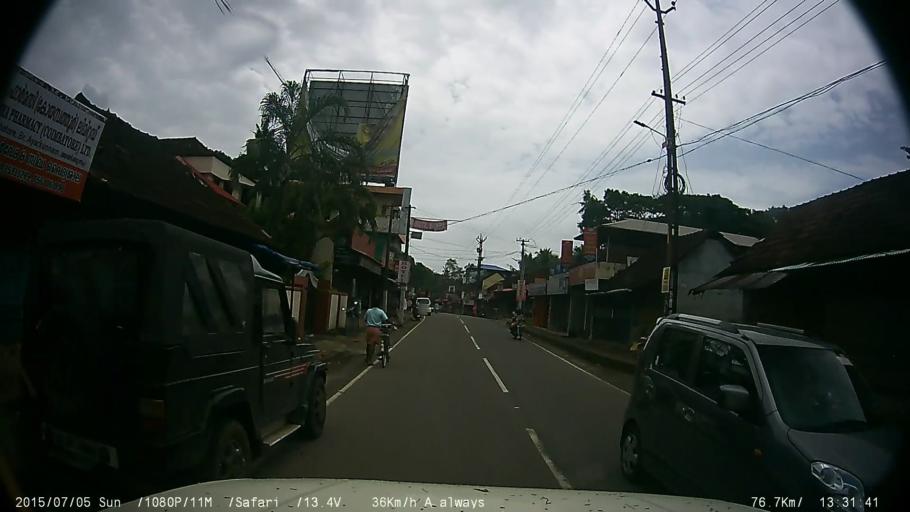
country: IN
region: Kerala
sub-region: Kottayam
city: Kottayam
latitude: 9.6372
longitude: 76.6064
